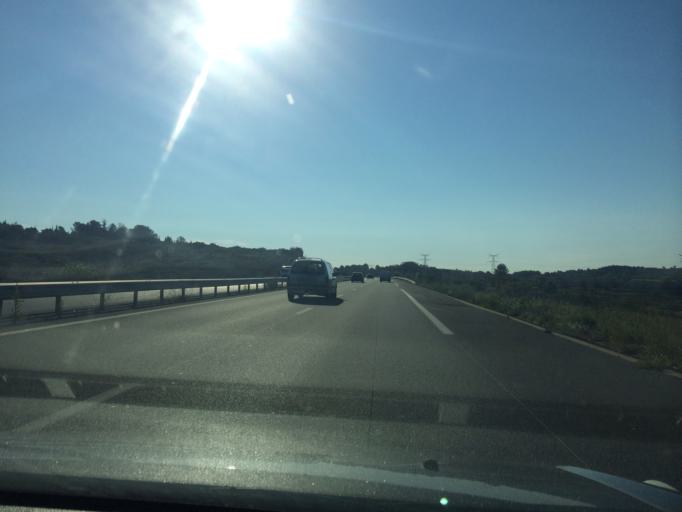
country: FR
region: Languedoc-Roussillon
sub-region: Departement de l'Herault
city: Murviel-les-Montpellier
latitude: 43.6327
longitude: 3.7358
